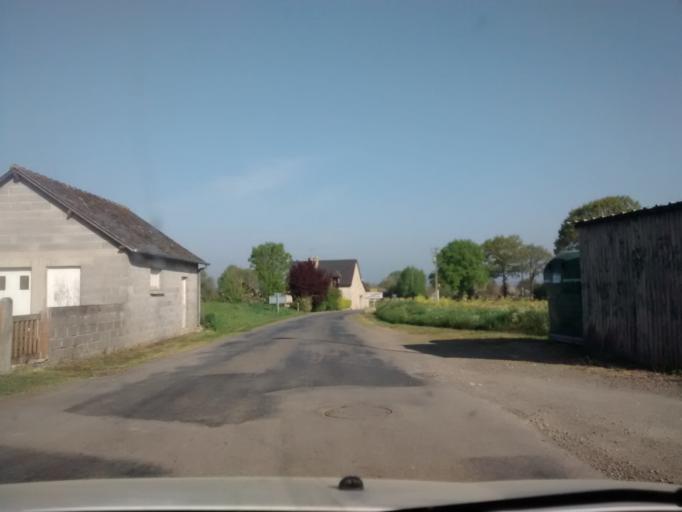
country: FR
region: Brittany
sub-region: Departement d'Ille-et-Vilaine
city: Romagne
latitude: 48.2760
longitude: -1.2905
